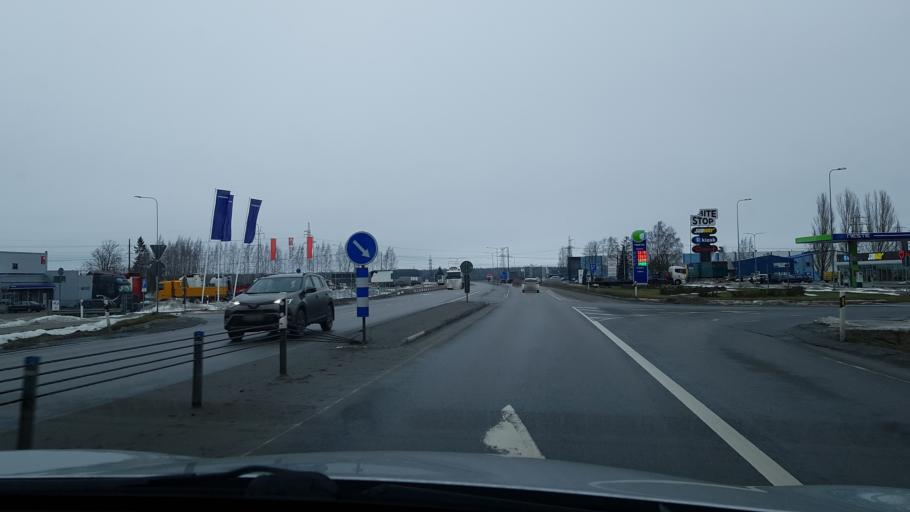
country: EE
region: Tartu
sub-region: Tartu linn
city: Tartu
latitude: 58.3743
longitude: 26.6780
